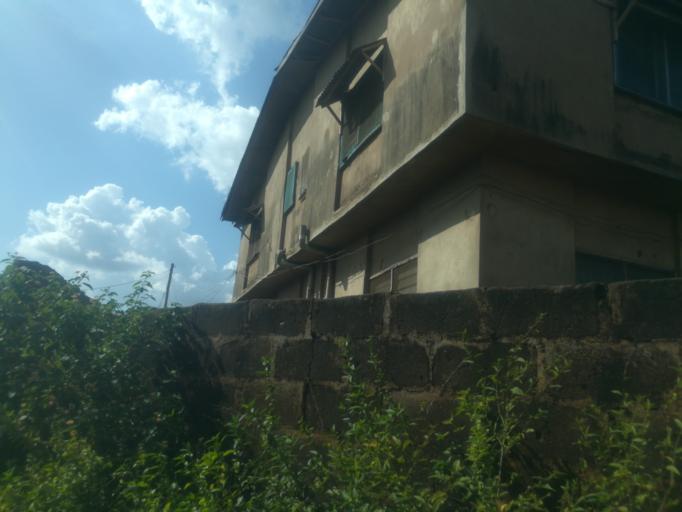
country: NG
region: Oyo
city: Ibadan
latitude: 7.4230
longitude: 3.9719
